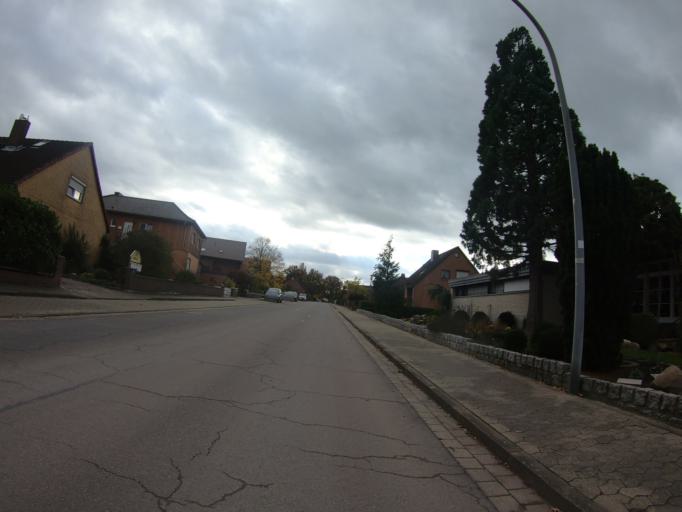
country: DE
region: Lower Saxony
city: Adenbuettel
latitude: 52.3792
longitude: 10.4831
